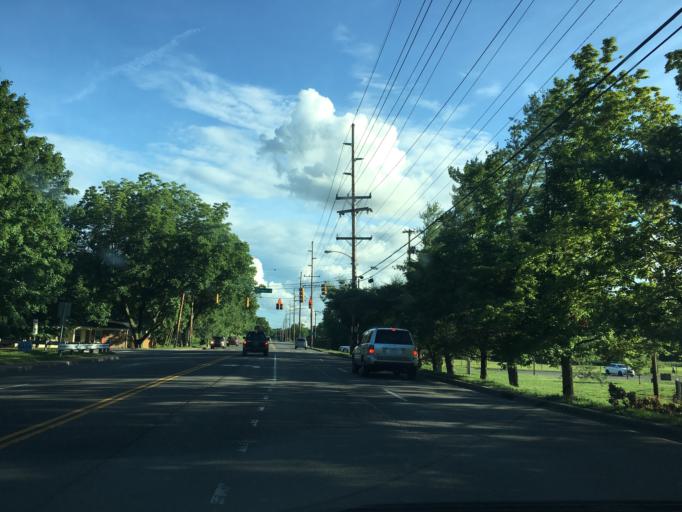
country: US
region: Tennessee
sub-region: Davidson County
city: Oak Hill
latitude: 36.0665
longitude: -86.7380
